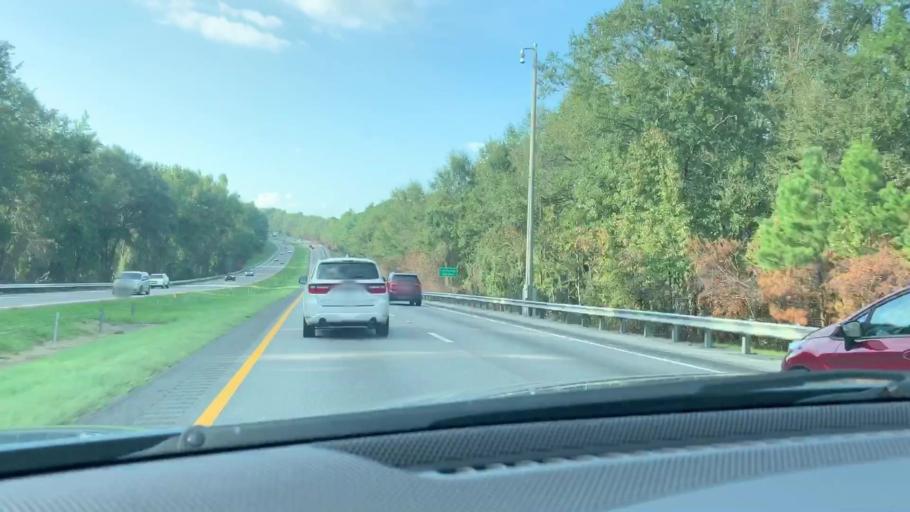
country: US
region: South Carolina
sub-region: Calhoun County
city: Oak Grove
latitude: 33.7494
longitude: -80.9430
